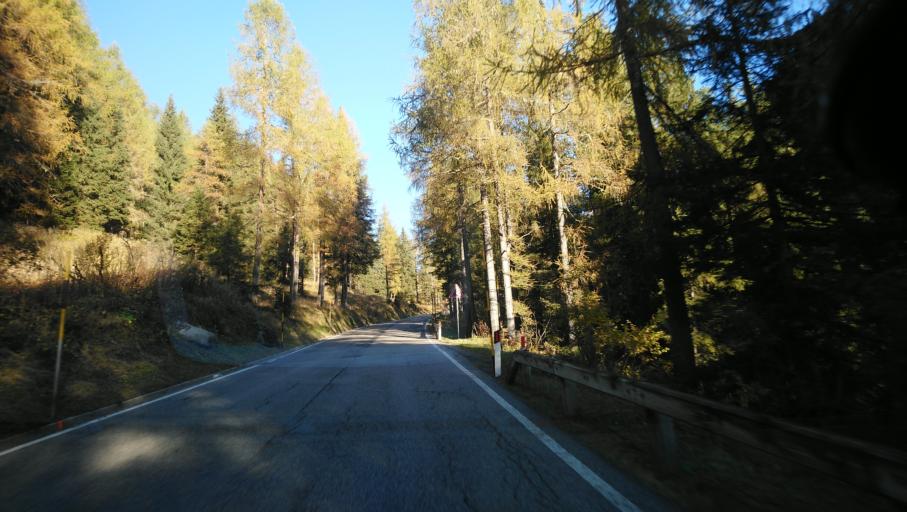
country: IT
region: Veneto
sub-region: Provincia di Belluno
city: Falcade Alto
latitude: 46.3686
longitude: 11.8279
